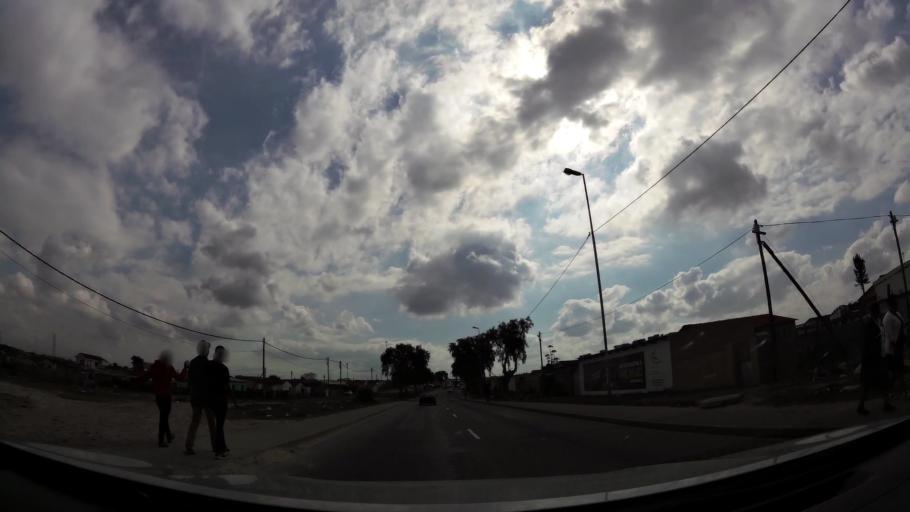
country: ZA
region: Eastern Cape
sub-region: Nelson Mandela Bay Metropolitan Municipality
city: Port Elizabeth
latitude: -33.8038
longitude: 25.5886
